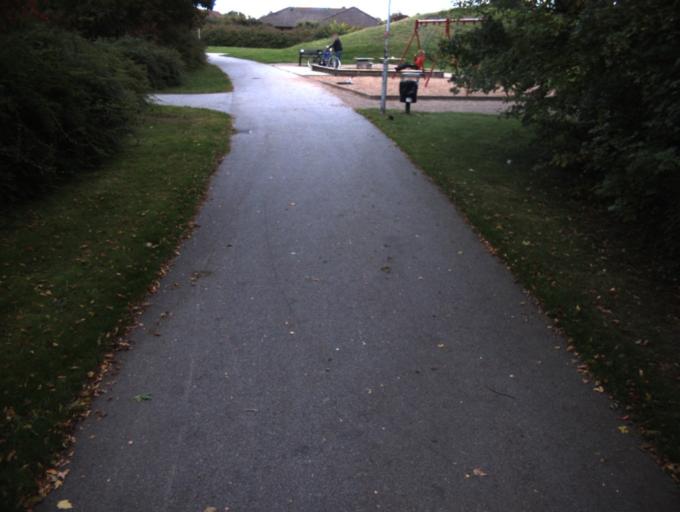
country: SE
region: Skane
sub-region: Helsingborg
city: Odakra
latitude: 56.1056
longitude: 12.7562
